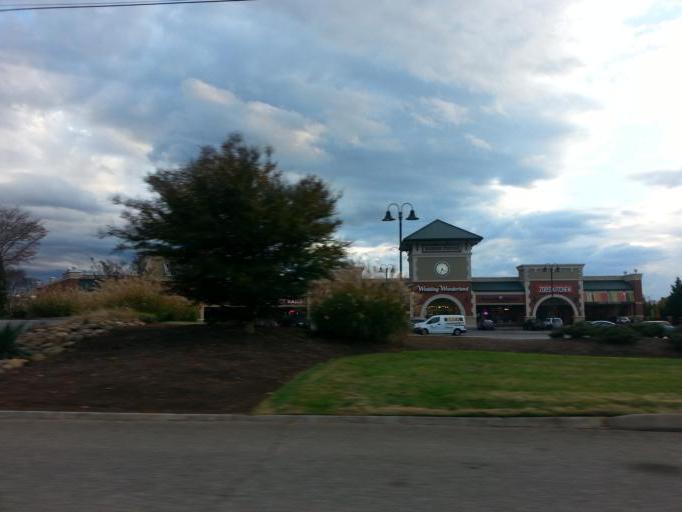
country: US
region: Tennessee
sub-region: Knox County
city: Knoxville
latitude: 35.9318
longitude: -84.0130
